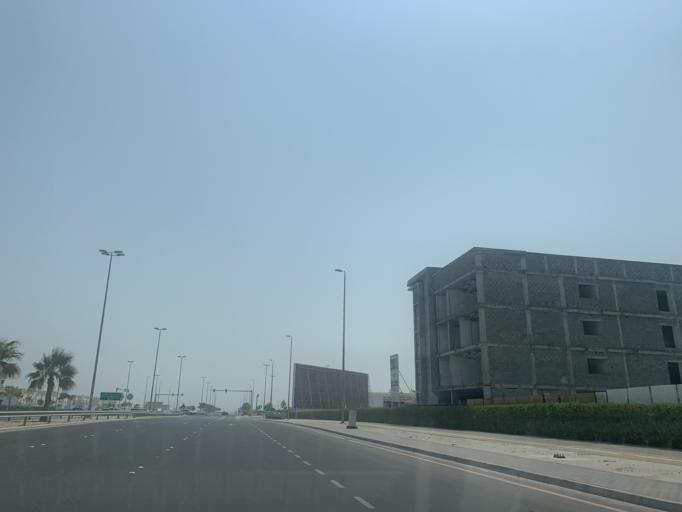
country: BH
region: Muharraq
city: Al Muharraq
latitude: 26.3081
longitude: 50.6297
